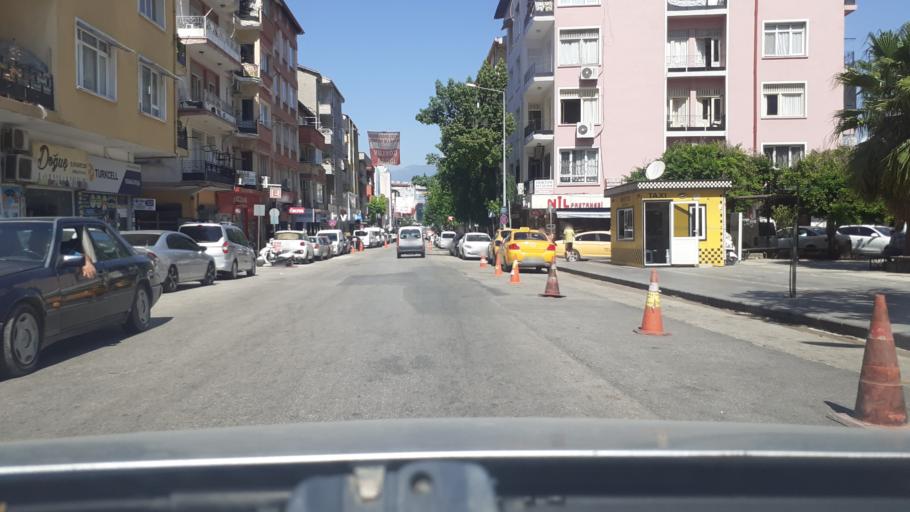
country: TR
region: Hatay
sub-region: Antakya Ilcesi
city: Antakya
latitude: 36.2015
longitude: 36.1649
